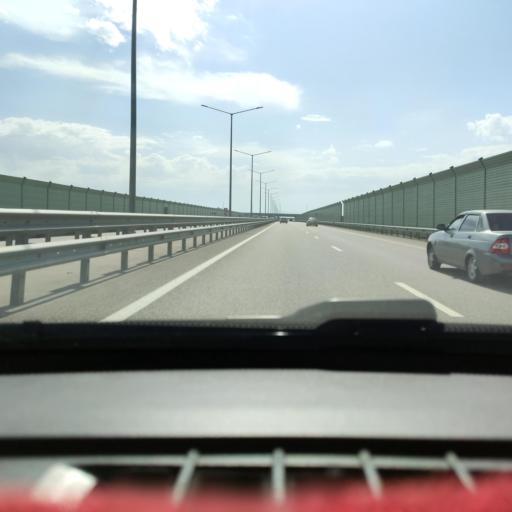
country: RU
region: Voronezj
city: Novaya Usman'
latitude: 51.6043
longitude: 39.3329
